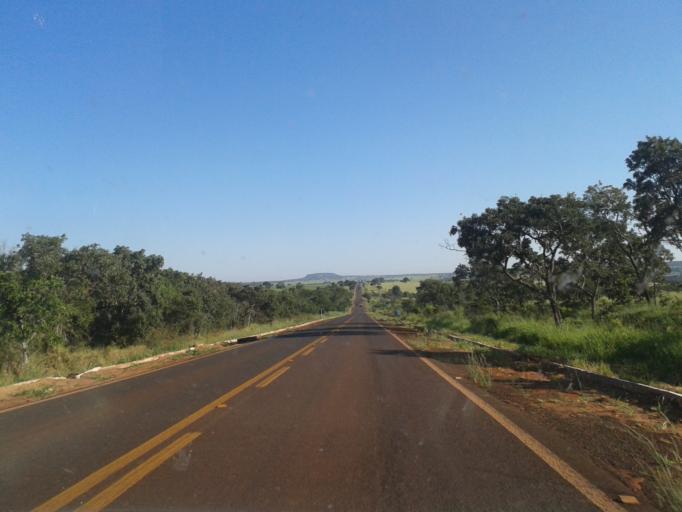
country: BR
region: Minas Gerais
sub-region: Ituiutaba
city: Ituiutaba
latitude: -18.8522
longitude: -49.4756
